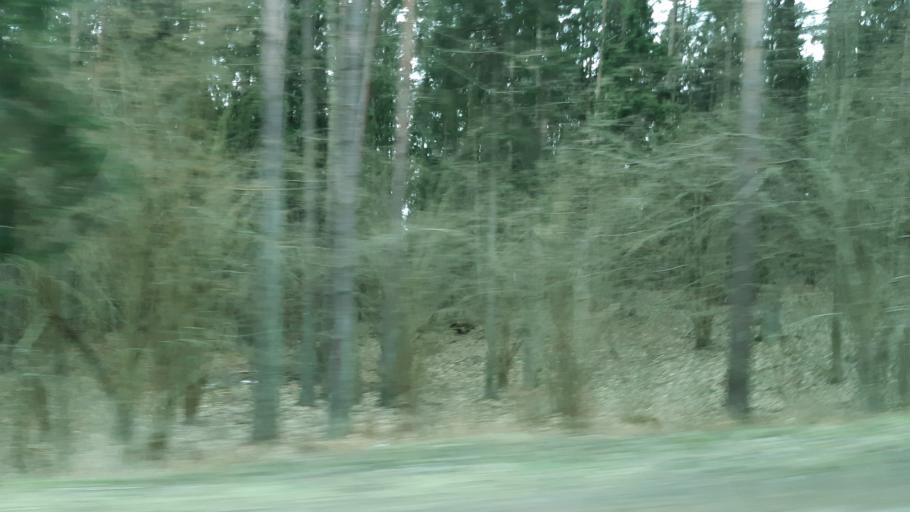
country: PL
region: Podlasie
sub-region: Suwalki
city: Suwalki
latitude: 54.2801
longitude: 22.9459
